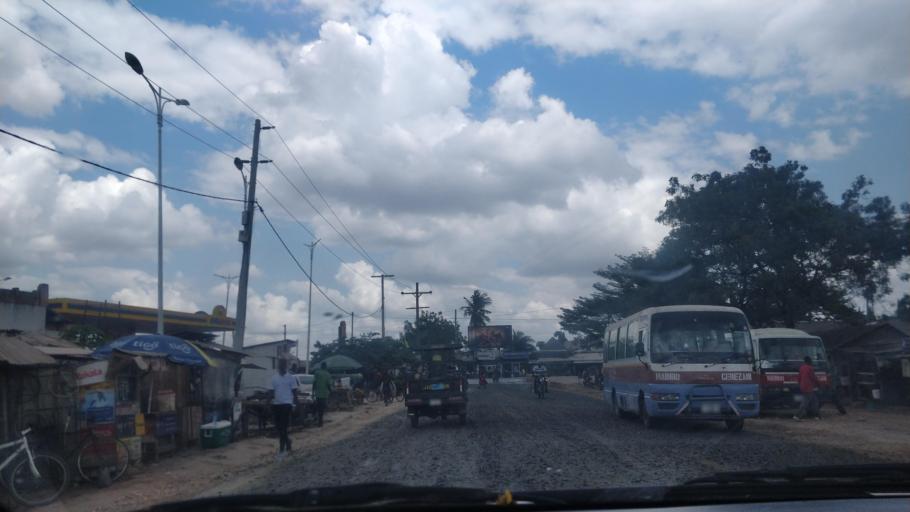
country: TZ
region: Dar es Salaam
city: Magomeni
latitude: -6.8084
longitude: 39.2223
